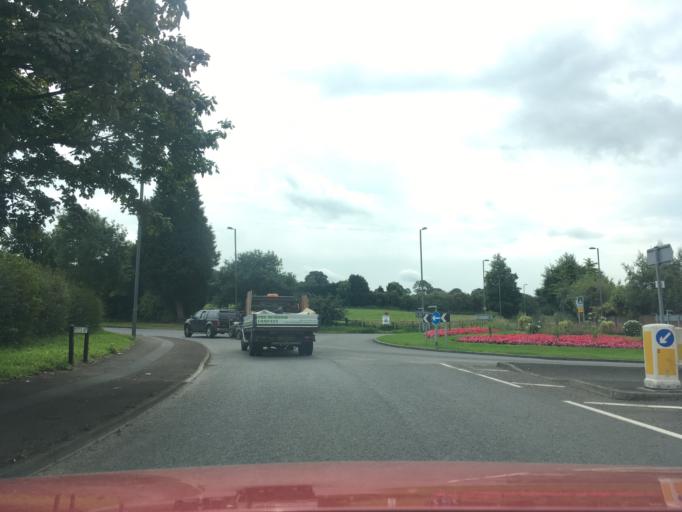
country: GB
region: England
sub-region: South Gloucestershire
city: Thornbury
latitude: 51.6033
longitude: -2.5059
